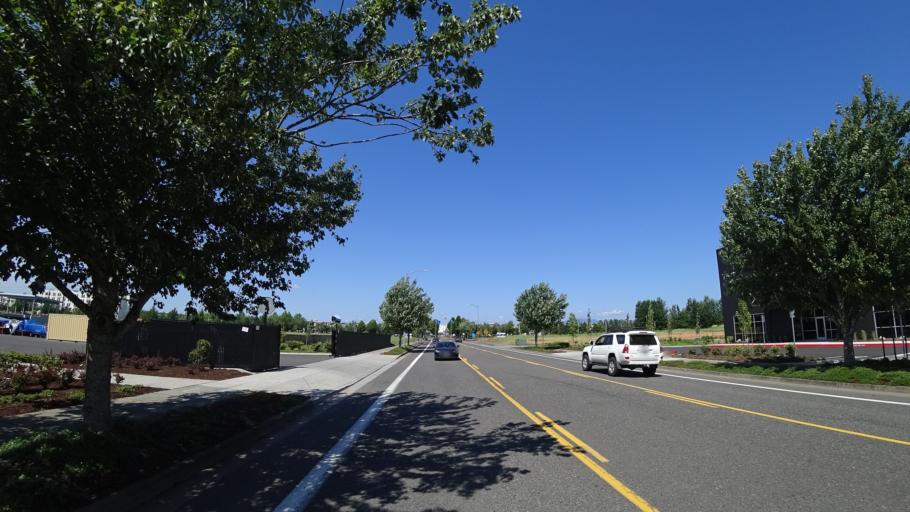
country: US
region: Oregon
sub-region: Multnomah County
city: Lents
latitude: 45.5706
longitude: -122.5594
